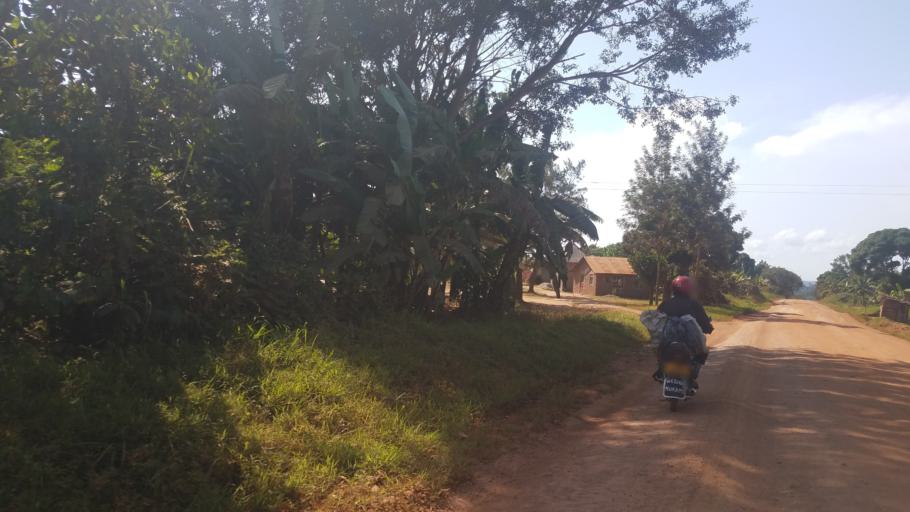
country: UG
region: Central Region
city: Masaka
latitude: -0.3221
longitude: 31.6906
